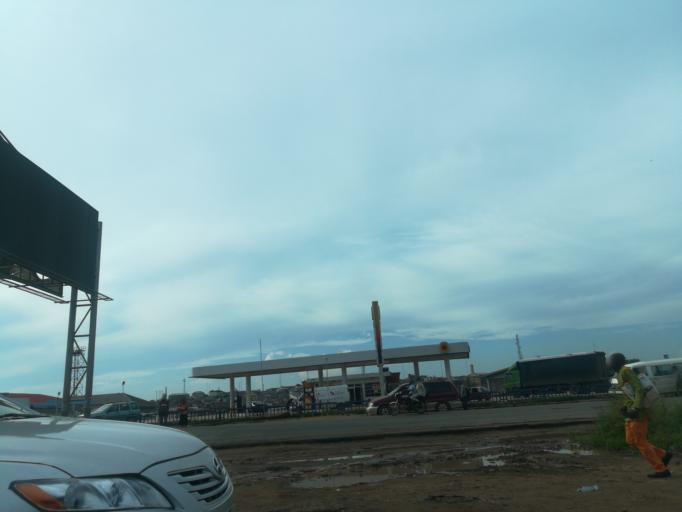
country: NG
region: Oyo
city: Ibadan
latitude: 7.3998
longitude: 3.9401
